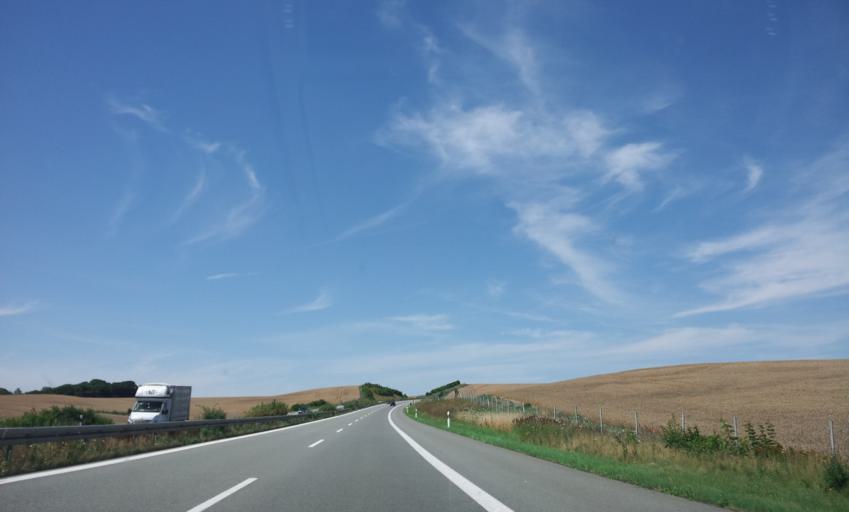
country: DE
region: Mecklenburg-Vorpommern
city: Neuenkirchen
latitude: 53.5907
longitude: 13.4001
